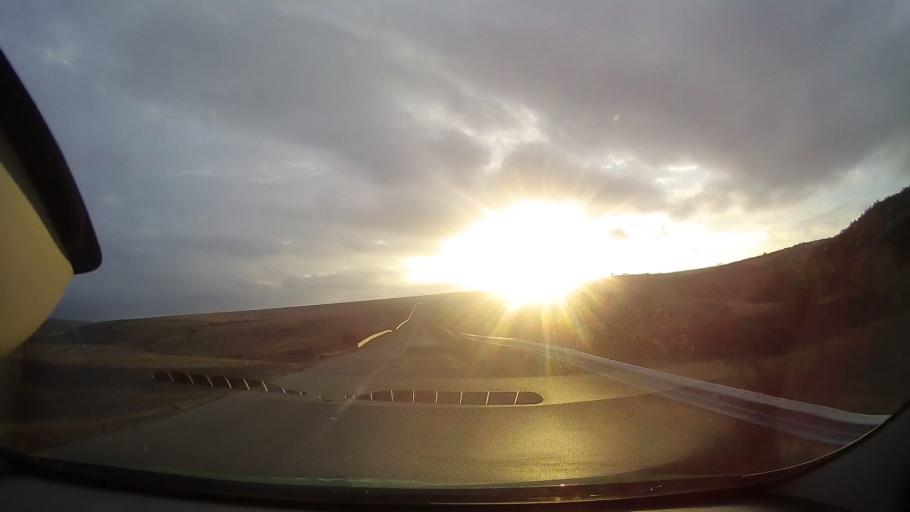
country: RO
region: Constanta
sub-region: Comuna Adamclisi
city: Adamclisi
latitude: 44.0386
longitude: 27.9414
